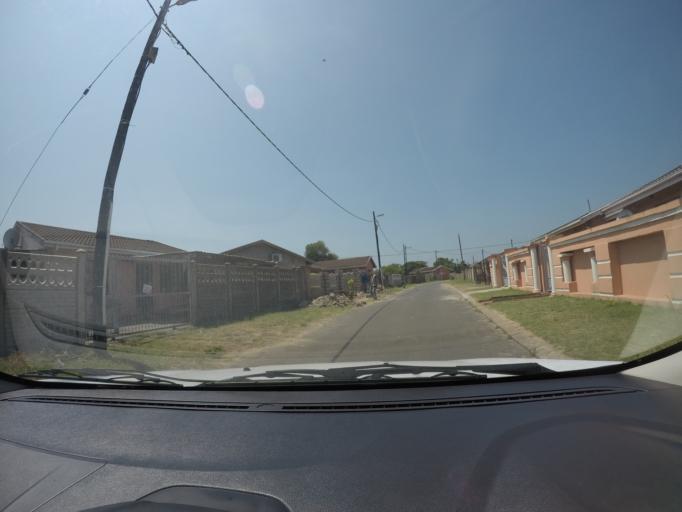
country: ZA
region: KwaZulu-Natal
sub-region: uThungulu District Municipality
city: eSikhawini
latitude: -28.8682
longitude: 31.9261
